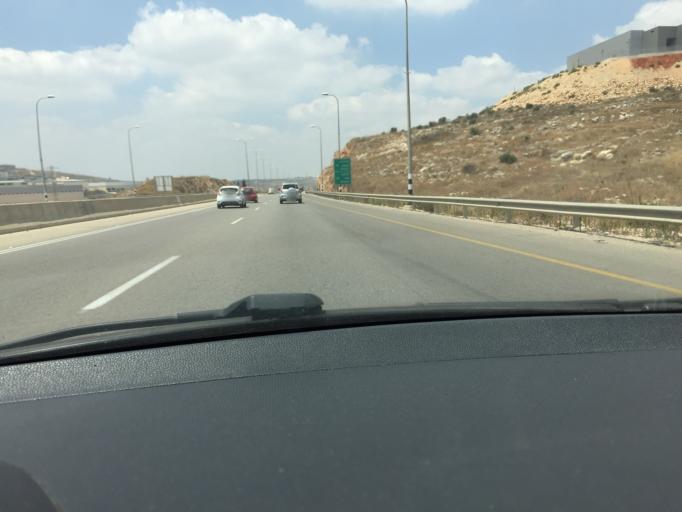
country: IL
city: Revava
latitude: 32.1029
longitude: 35.1257
